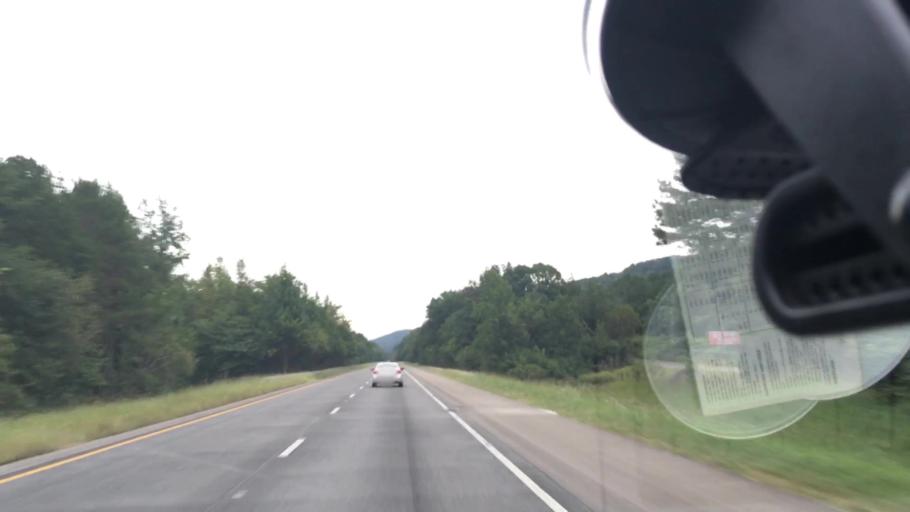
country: US
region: Alabama
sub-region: DeKalb County
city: Collinsville
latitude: 34.3182
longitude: -85.8470
